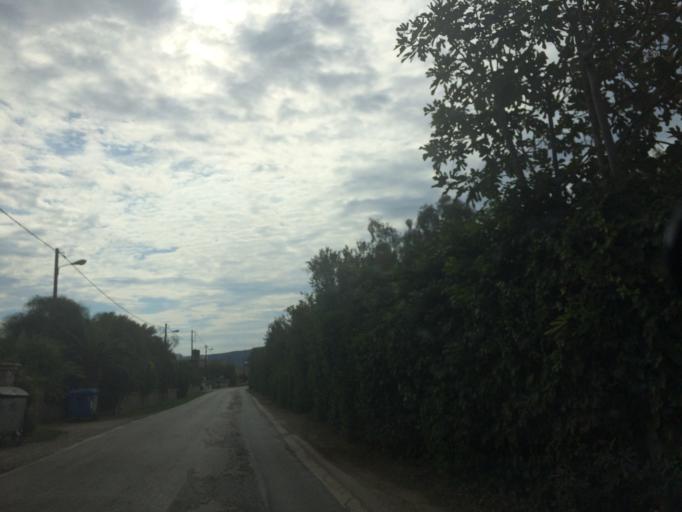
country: GR
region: Peloponnese
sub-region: Nomos Messinias
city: Pylos
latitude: 36.9478
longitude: 21.7064
